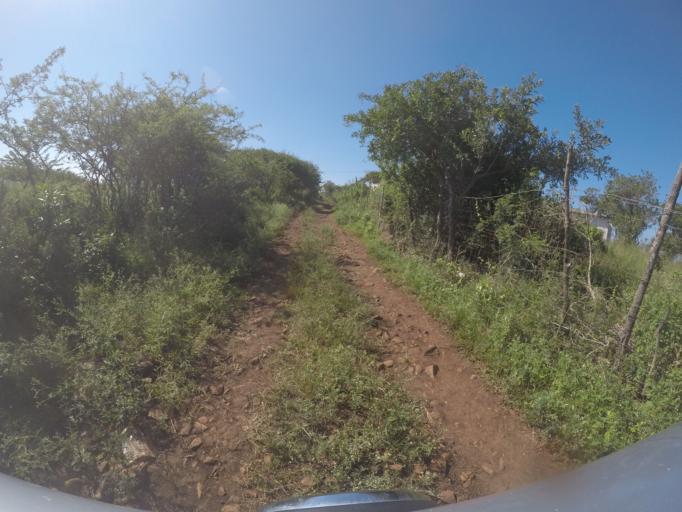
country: ZA
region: KwaZulu-Natal
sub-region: uThungulu District Municipality
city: Empangeni
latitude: -28.5715
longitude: 31.7102
